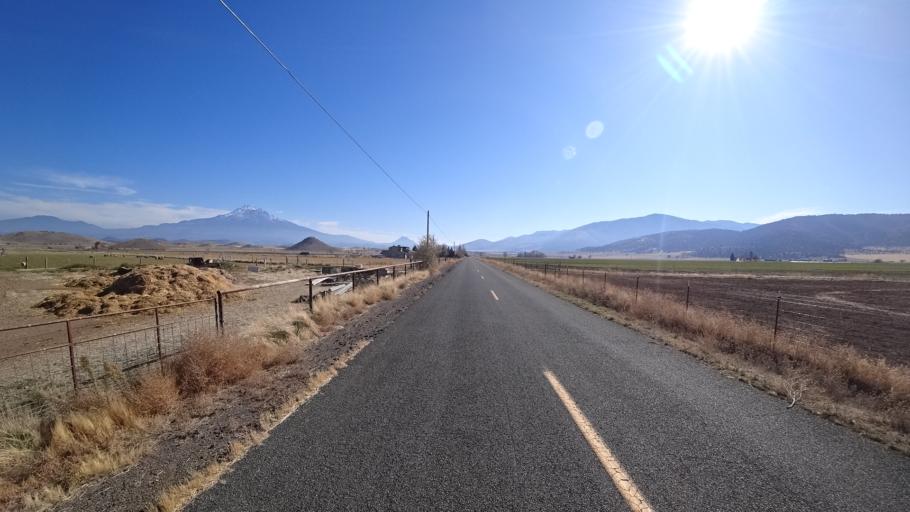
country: US
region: California
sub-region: Siskiyou County
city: Montague
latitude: 41.5456
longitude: -122.5407
